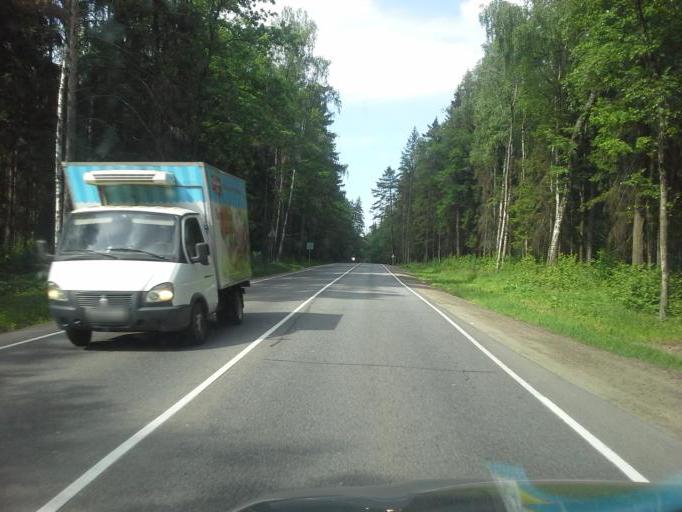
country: RU
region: Moskovskaya
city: Odintsovo
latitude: 55.7025
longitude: 37.2250
